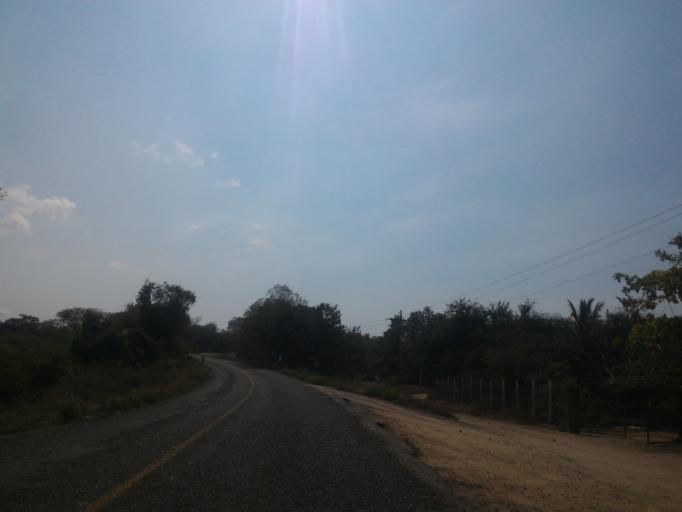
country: MX
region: Michoacan
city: Coahuayana Viejo
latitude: 18.3875
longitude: -103.5248
